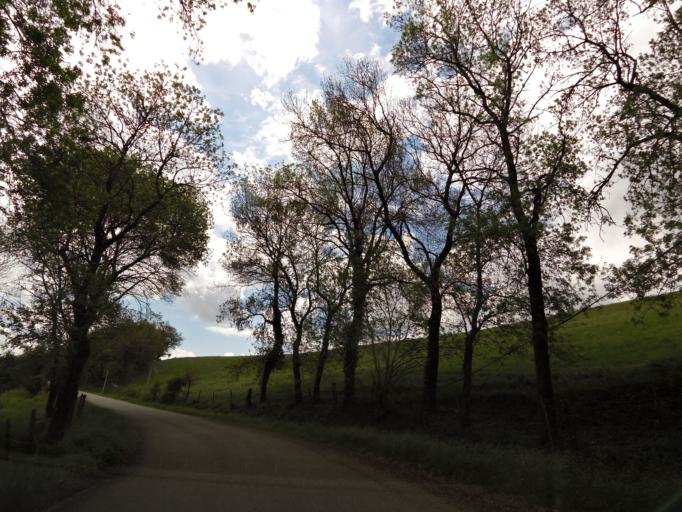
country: FR
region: Languedoc-Roussillon
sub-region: Departement de l'Aude
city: Villepinte
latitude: 43.3508
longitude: 2.0772
